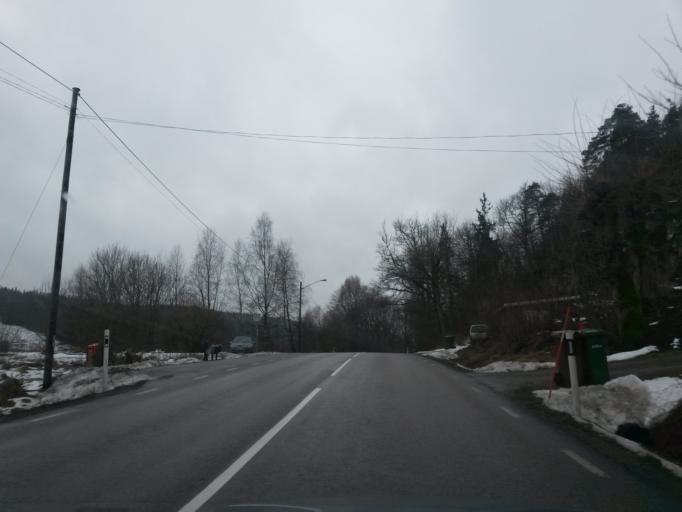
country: SE
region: Vaestra Goetaland
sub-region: Vanersborgs Kommun
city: Vargon
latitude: 58.3567
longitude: 12.4332
